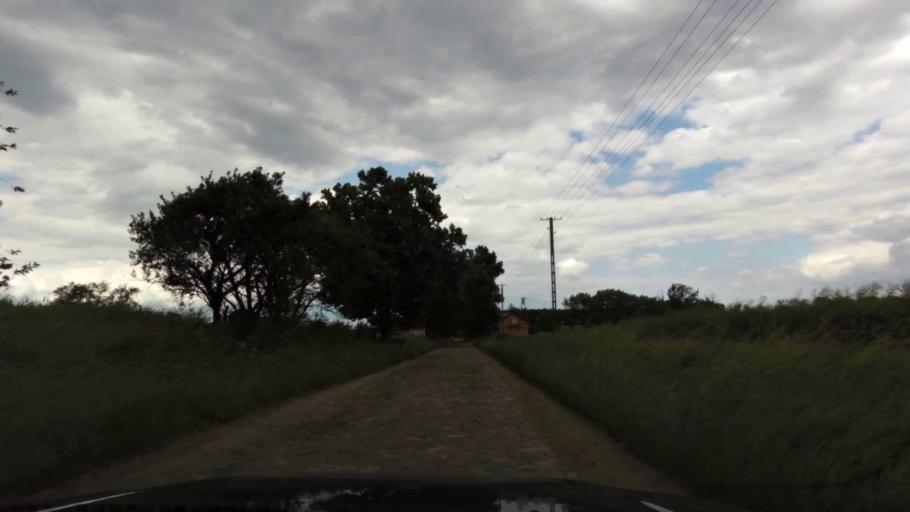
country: PL
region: West Pomeranian Voivodeship
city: Trzcinsko Zdroj
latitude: 52.9746
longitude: 14.7206
